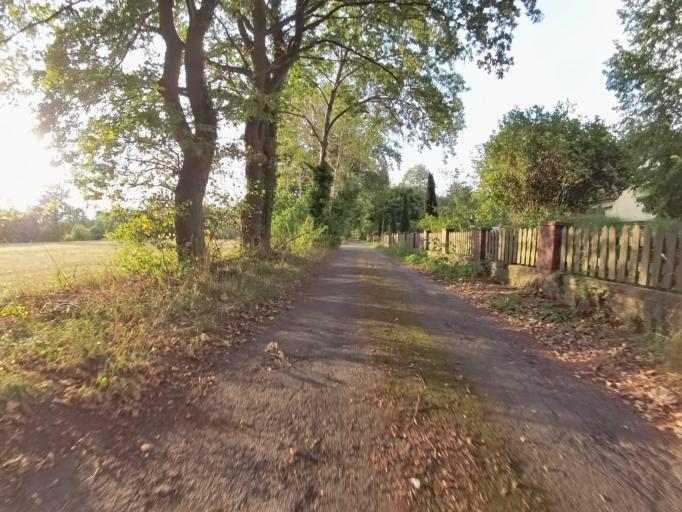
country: DE
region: North Rhine-Westphalia
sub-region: Regierungsbezirk Munster
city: Westerkappeln
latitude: 52.3631
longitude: 7.8951
